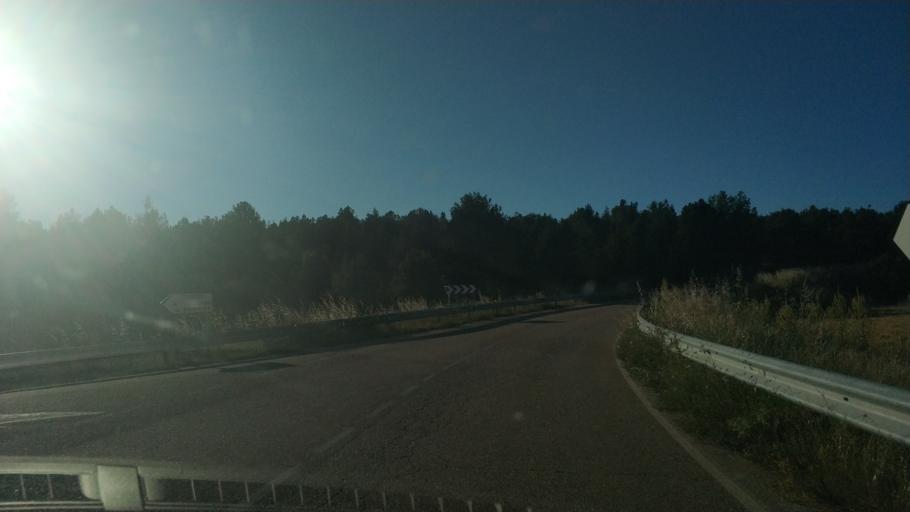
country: ES
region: Castille and Leon
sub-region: Provincia de Soria
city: Liceras
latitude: 41.4389
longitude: -3.2141
